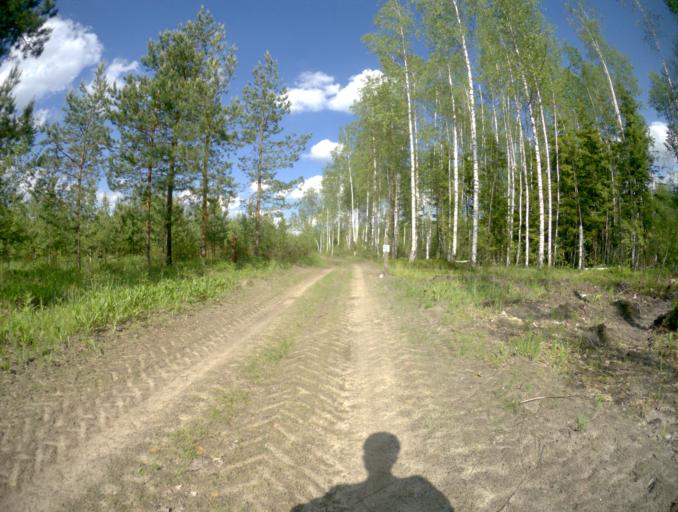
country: RU
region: Vladimir
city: Velikodvorskiy
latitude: 55.3189
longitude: 40.9256
